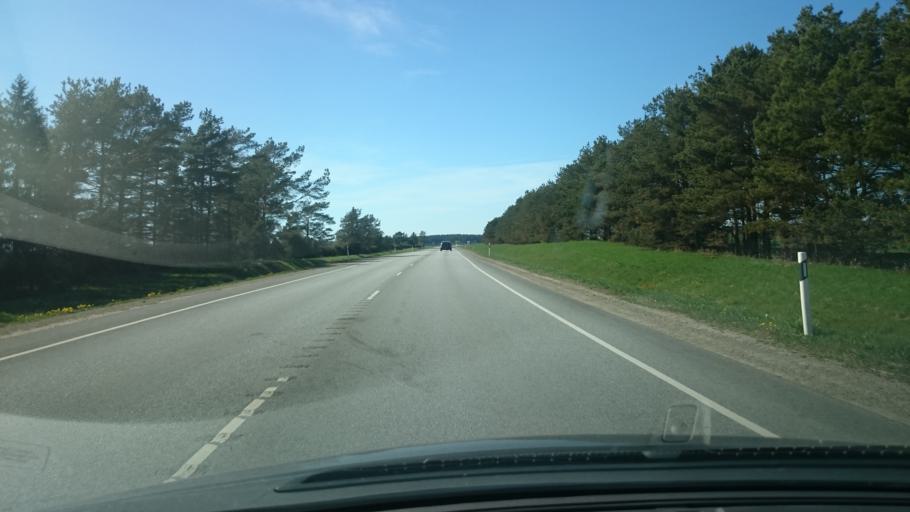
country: EE
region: Ida-Virumaa
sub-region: Puessi linn
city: Pussi
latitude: 59.4067
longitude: 27.0581
